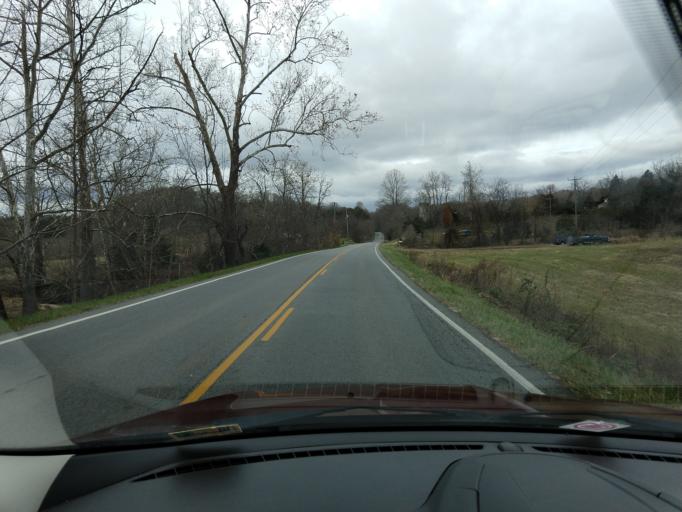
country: US
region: Virginia
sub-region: Botetourt County
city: Blue Ridge
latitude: 37.2623
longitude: -79.7519
